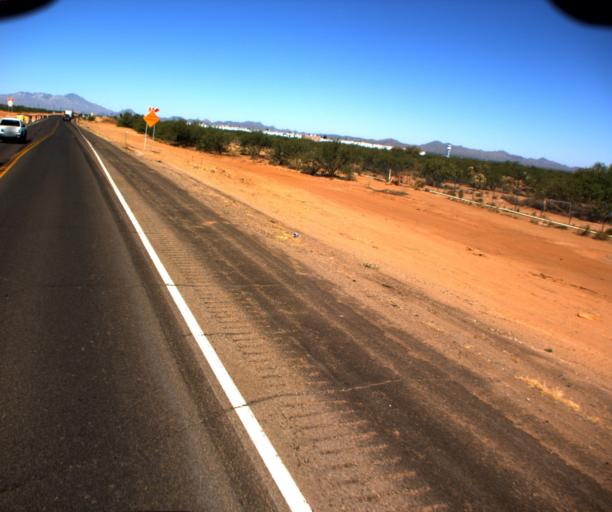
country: US
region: Arizona
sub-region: Pima County
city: Valencia West
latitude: 32.1373
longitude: -111.1612
